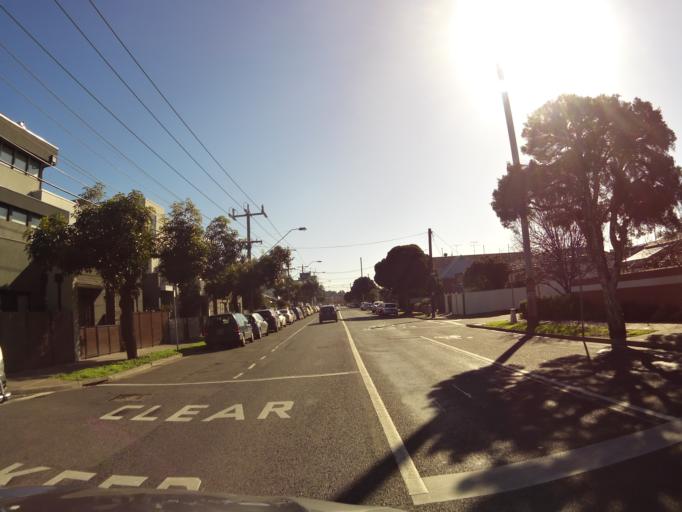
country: AU
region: Victoria
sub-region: Yarra
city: Richmond
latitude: -37.8227
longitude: 145.0077
